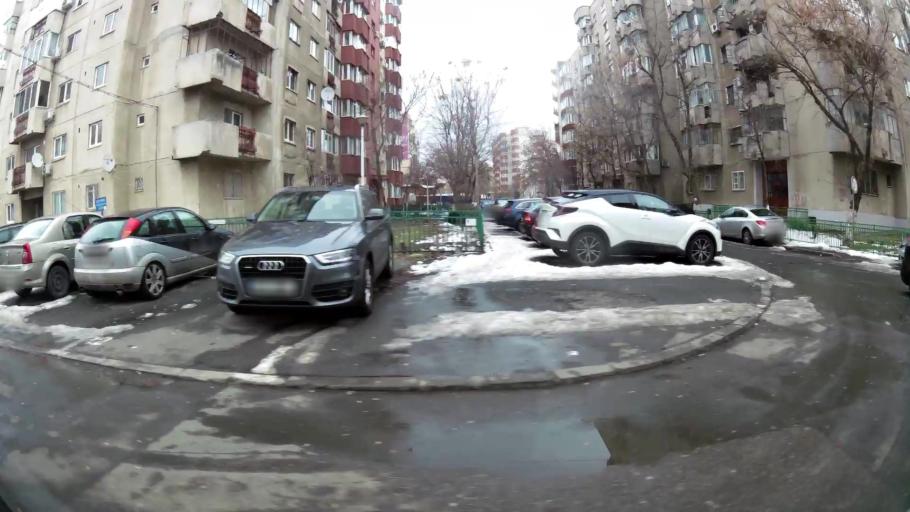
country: RO
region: Bucuresti
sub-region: Municipiul Bucuresti
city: Bucuresti
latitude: 44.4192
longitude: 26.0655
